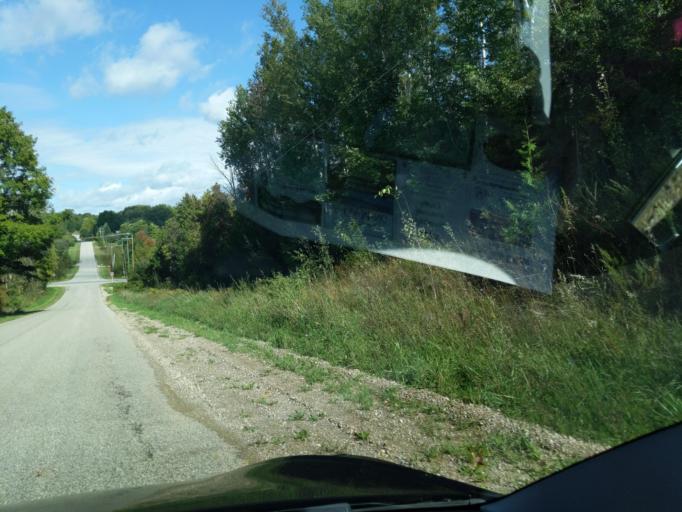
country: US
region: Michigan
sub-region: Antrim County
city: Elk Rapids
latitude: 44.9594
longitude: -85.3323
